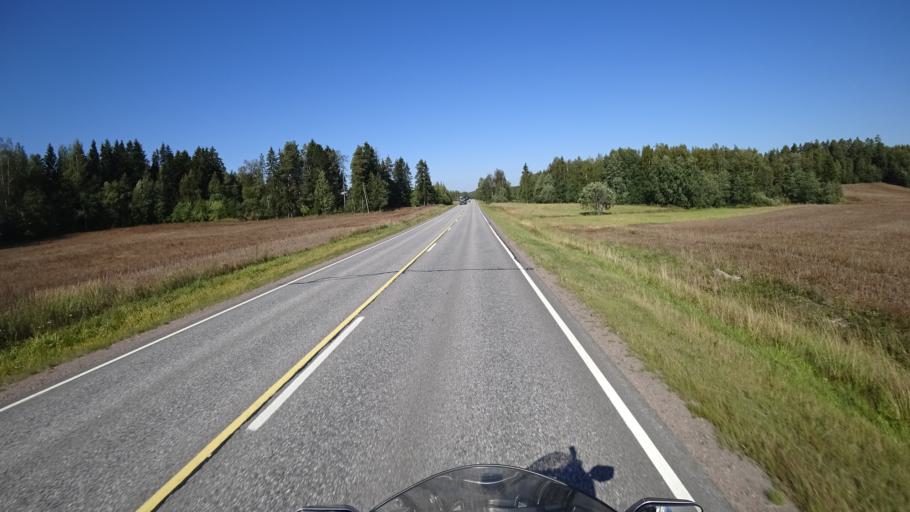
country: FI
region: Uusimaa
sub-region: Helsinki
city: Vihti
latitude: 60.4169
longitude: 24.4450
